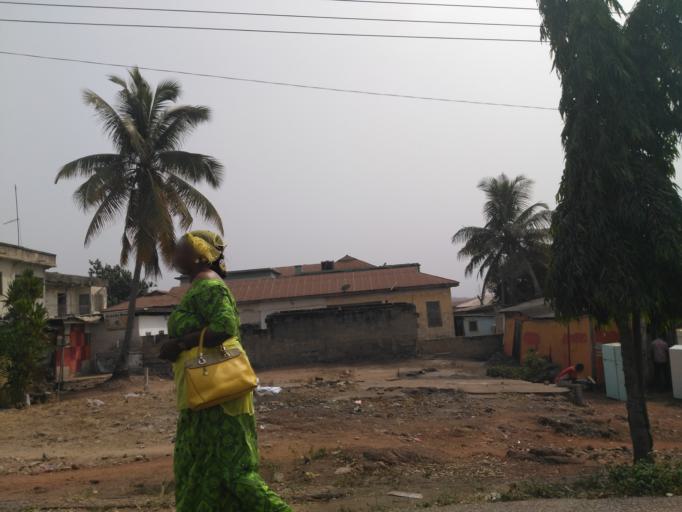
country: GH
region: Ashanti
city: Tafo
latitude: 6.7134
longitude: -1.6184
